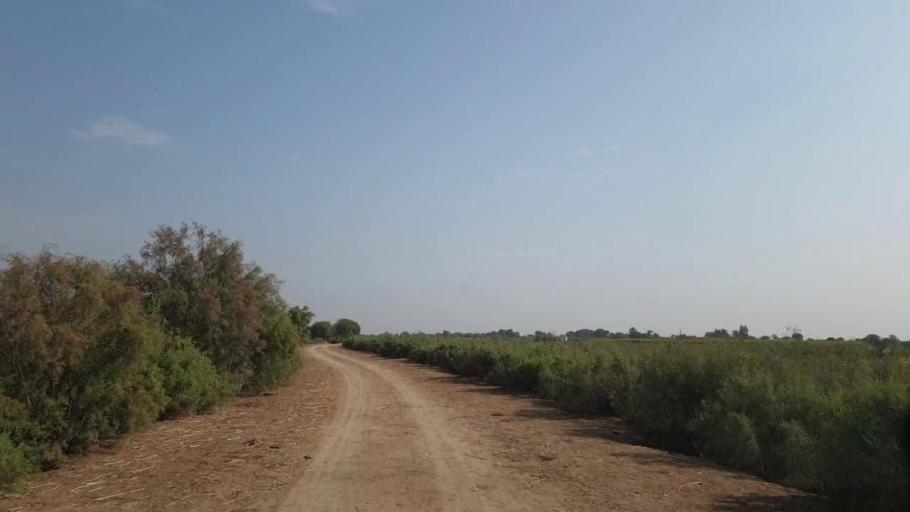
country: PK
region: Sindh
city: Tando Muhammad Khan
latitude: 25.0657
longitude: 68.4358
